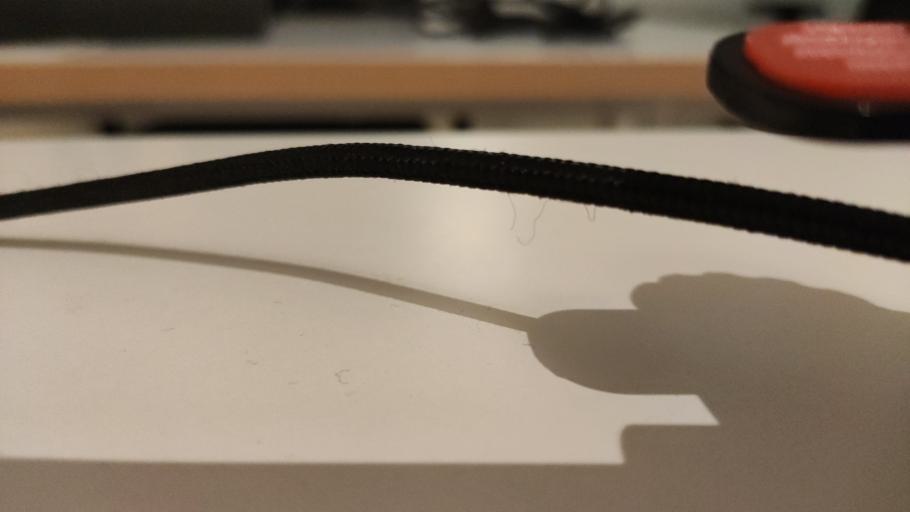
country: RU
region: Moskovskaya
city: Malino
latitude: 55.1019
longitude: 38.0773
